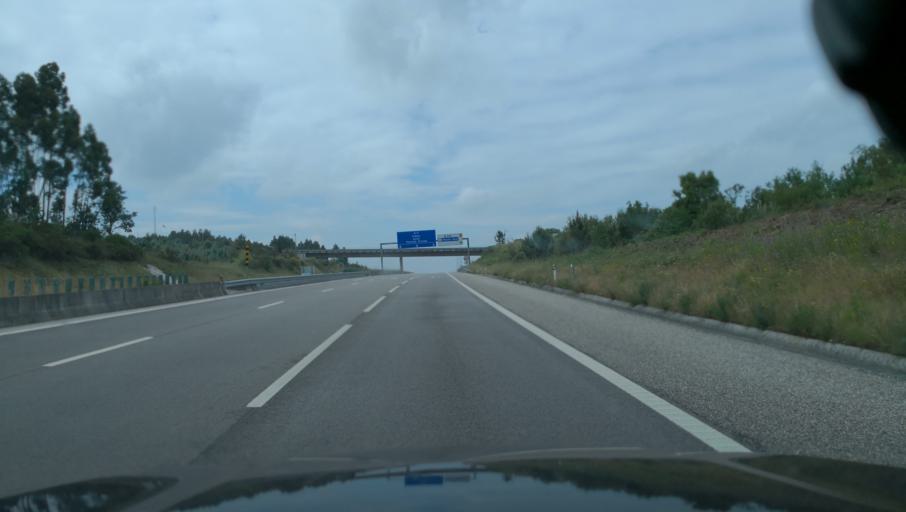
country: PT
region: Leiria
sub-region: Leiria
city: Souto da Carpalhosa
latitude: 39.8572
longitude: -8.8262
